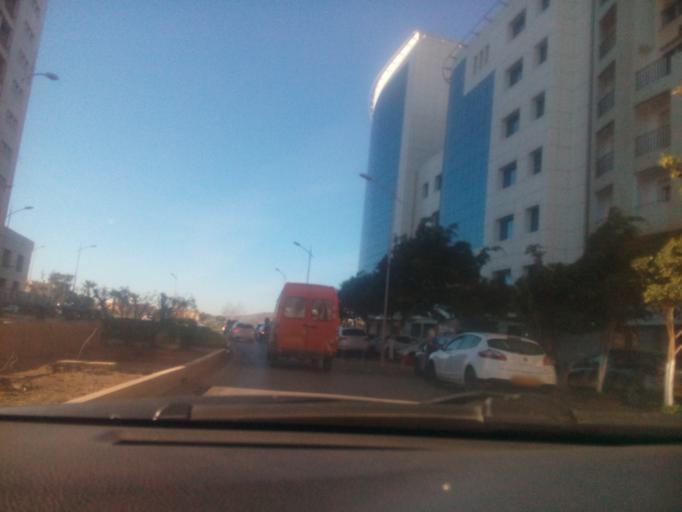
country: DZ
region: Oran
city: Oran
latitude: 35.7171
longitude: -0.6007
